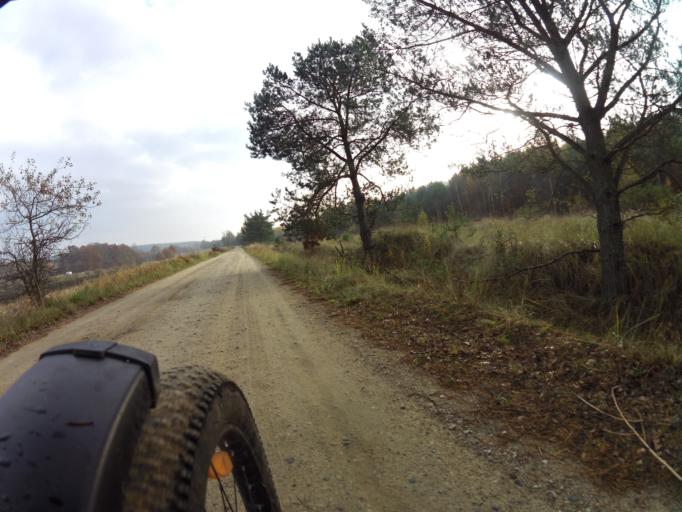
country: PL
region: Pomeranian Voivodeship
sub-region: Powiat wejherowski
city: Orle
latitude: 54.7010
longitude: 18.1103
